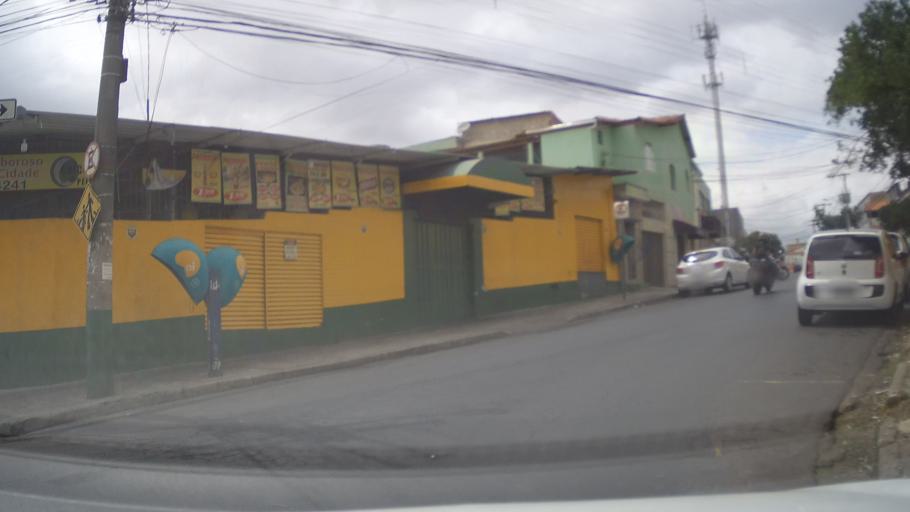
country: BR
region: Minas Gerais
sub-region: Belo Horizonte
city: Belo Horizonte
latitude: -19.8986
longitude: -43.9446
